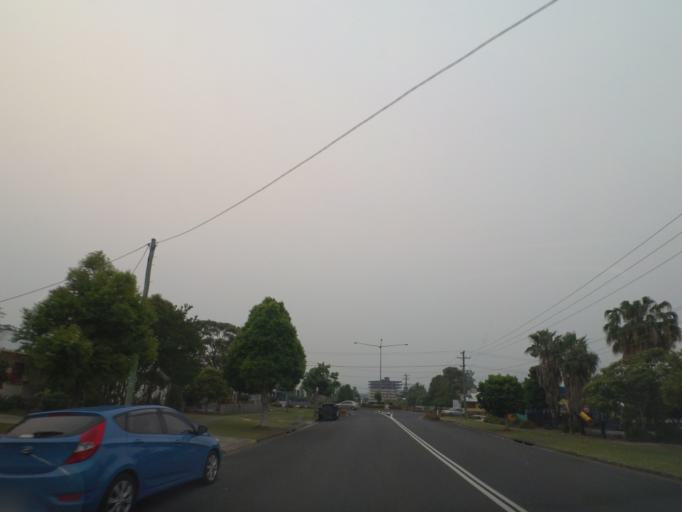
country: AU
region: New South Wales
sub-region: Coffs Harbour
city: Coffs Harbour
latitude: -30.3015
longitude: 153.1170
